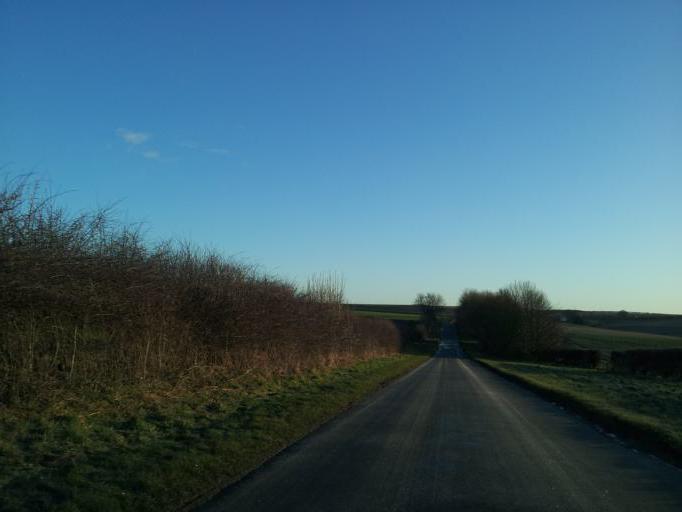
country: GB
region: England
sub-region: Lincolnshire
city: Horncastle
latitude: 53.2568
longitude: -0.1032
